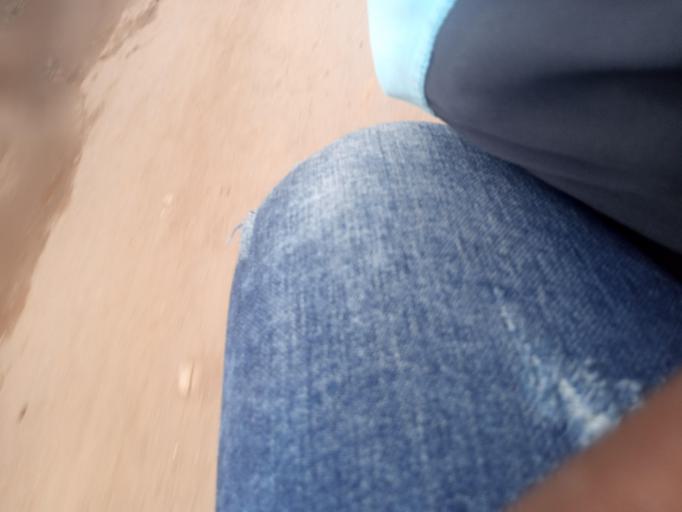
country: SL
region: Southern Province
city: Bo
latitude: 7.9675
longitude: -11.7372
